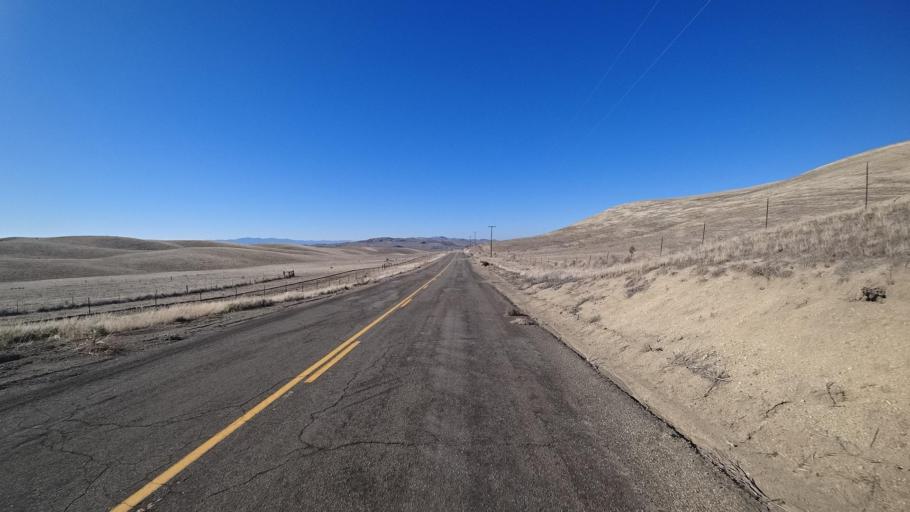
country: US
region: California
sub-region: Kern County
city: Maricopa
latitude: 34.9522
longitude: -119.4262
